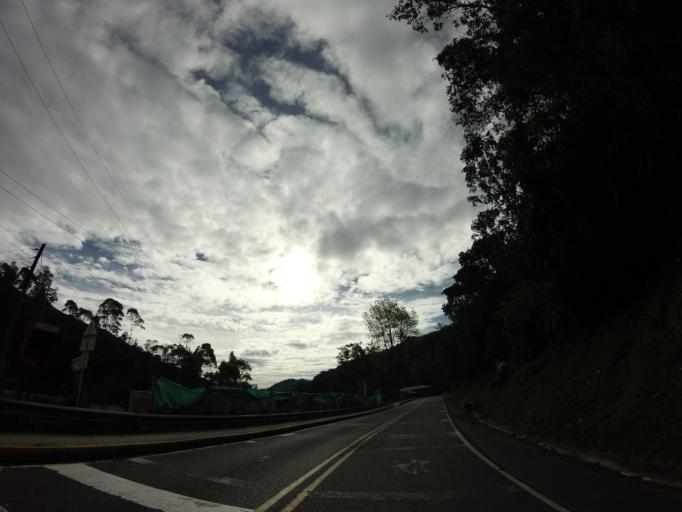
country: CO
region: Tolima
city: Herveo
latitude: 5.1342
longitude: -75.1928
